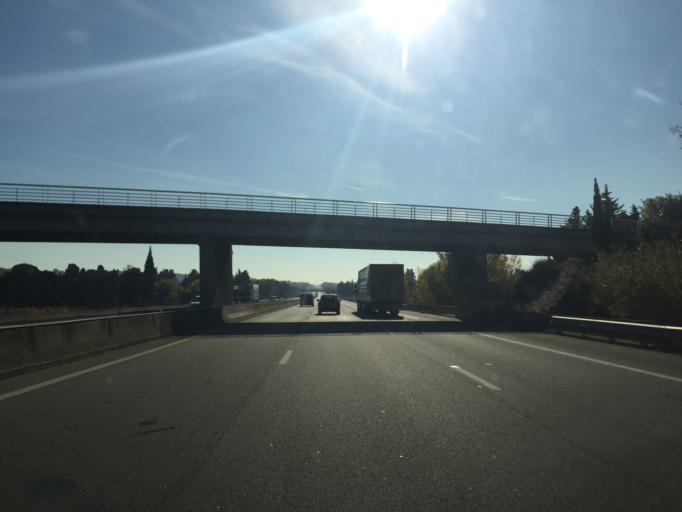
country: FR
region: Provence-Alpes-Cote d'Azur
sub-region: Departement du Vaucluse
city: Morieres-les-Avignon
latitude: 43.9435
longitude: 4.9112
